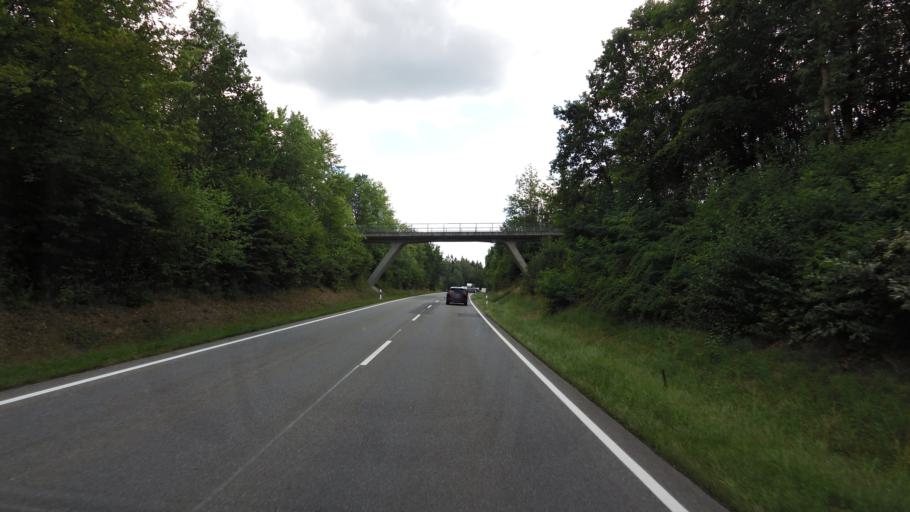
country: DE
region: Bavaria
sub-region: Lower Bavaria
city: Stallwang
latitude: 49.0467
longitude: 12.6490
